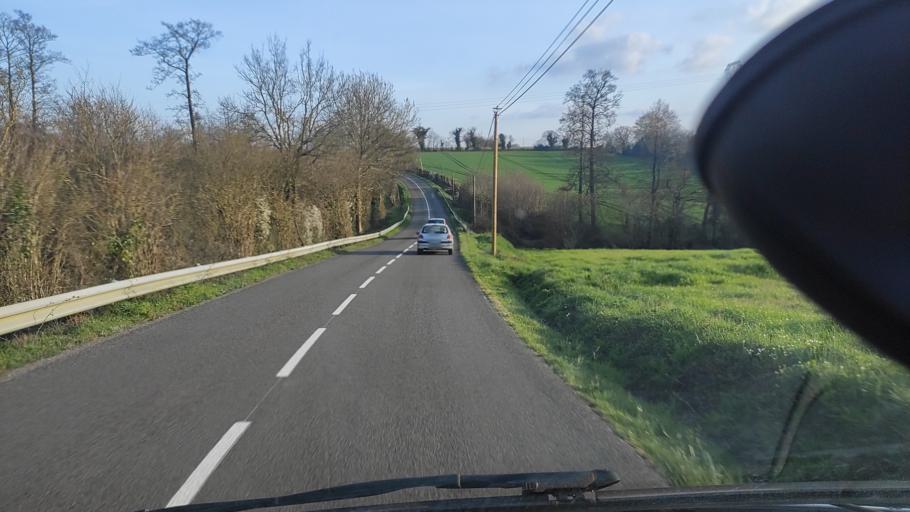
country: FR
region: Pays de la Loire
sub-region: Departement de la Vendee
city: La Chaize-le-Vicomte
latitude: 46.6541
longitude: -1.2982
